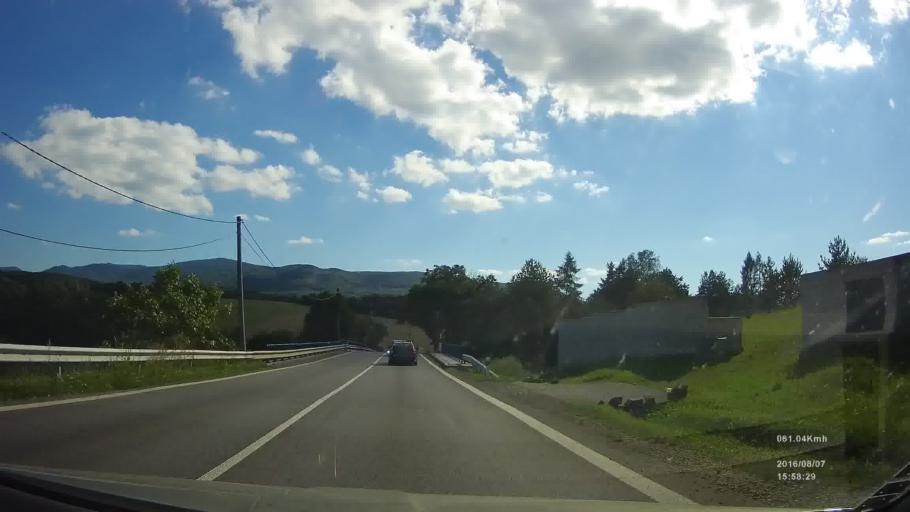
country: SK
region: Presovsky
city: Giraltovce
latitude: 49.0488
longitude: 21.4159
